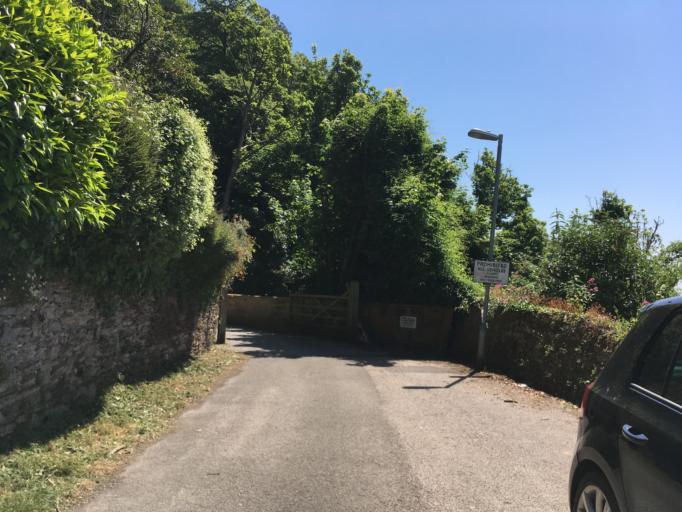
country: GB
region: England
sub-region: Devon
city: Dartmouth
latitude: 50.3470
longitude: -3.5665
